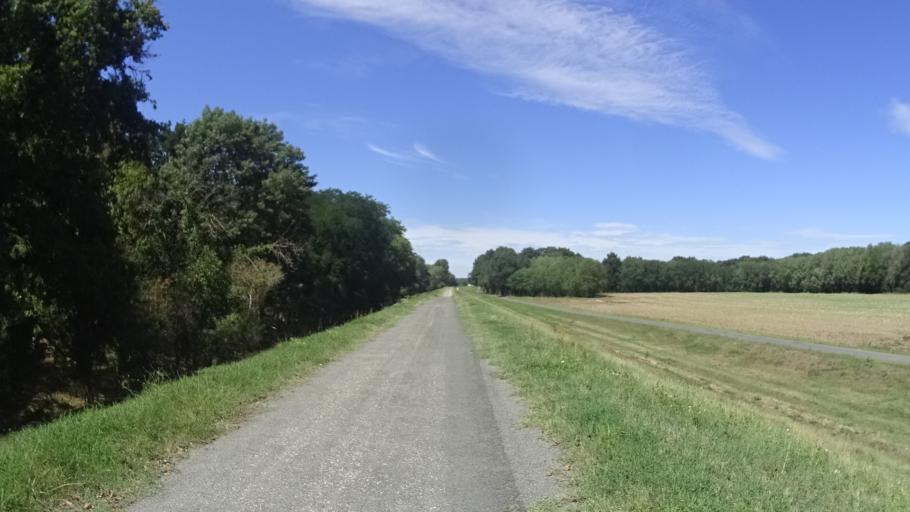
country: FR
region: Centre
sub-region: Departement du Loiret
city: Briare
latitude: 47.5925
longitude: 2.7747
